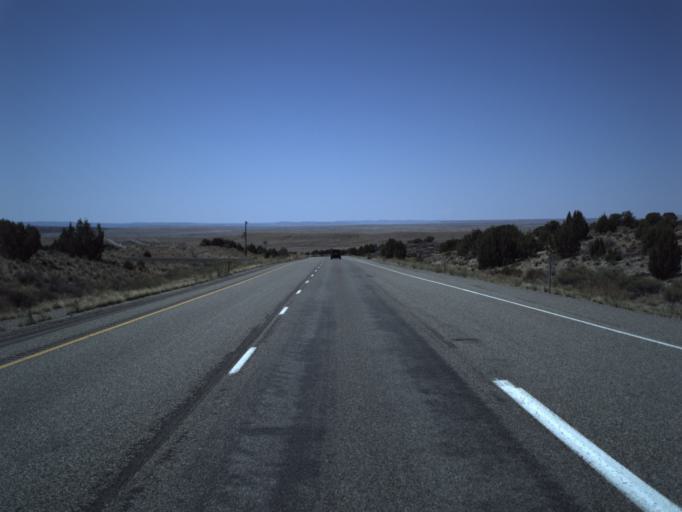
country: US
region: Colorado
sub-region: Mesa County
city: Loma
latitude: 39.1681
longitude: -109.1347
